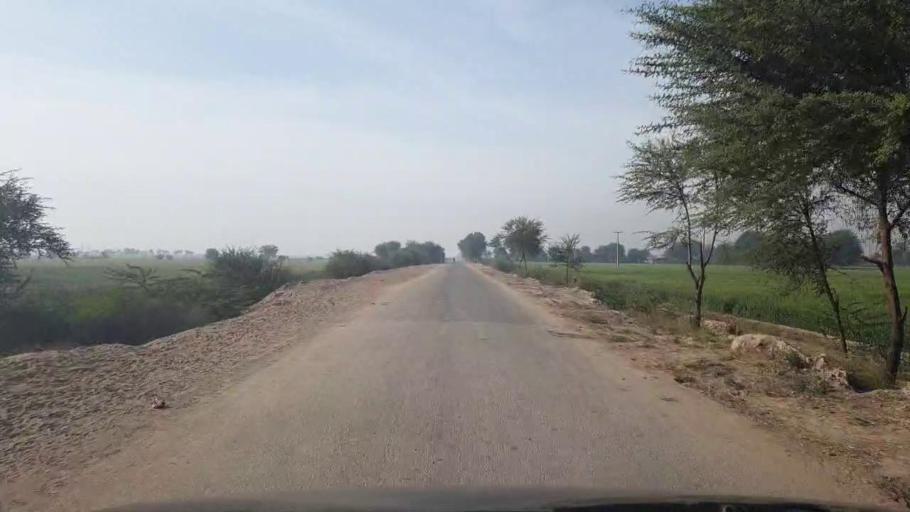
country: PK
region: Sindh
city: Umarkot
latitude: 25.3650
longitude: 69.7038
